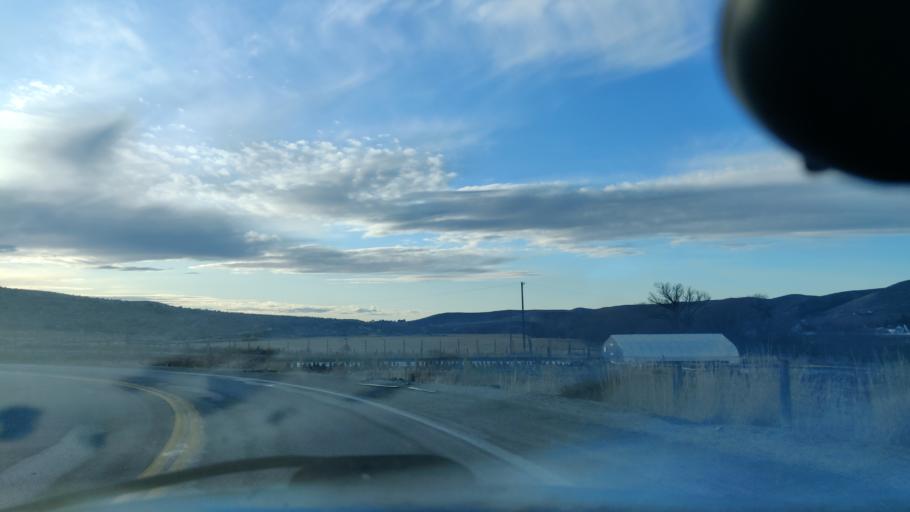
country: US
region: Idaho
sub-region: Ada County
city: Eagle
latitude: 43.7303
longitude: -116.2883
